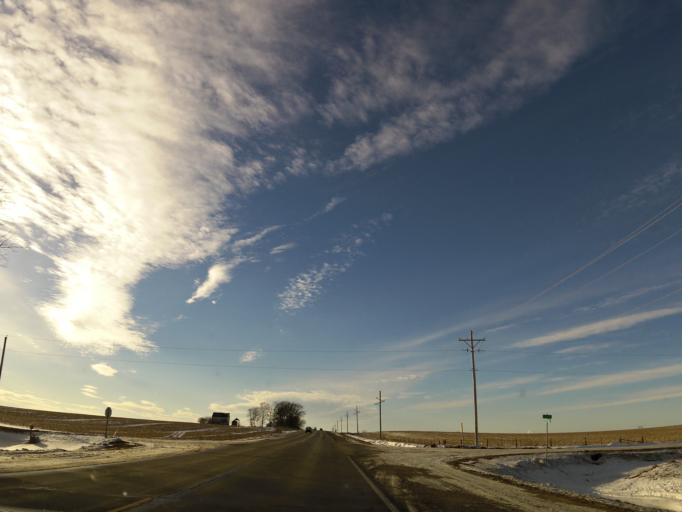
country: US
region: Iowa
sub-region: Butler County
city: Shell Rock
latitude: 42.7150
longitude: -92.5438
